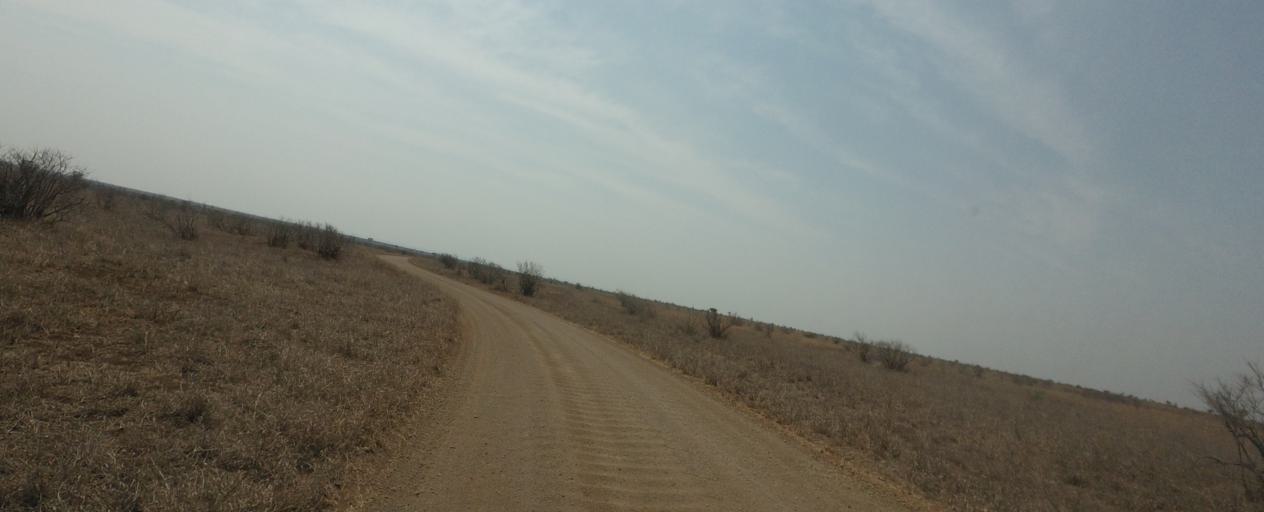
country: ZA
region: Limpopo
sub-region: Mopani District Municipality
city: Phalaborwa
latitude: -24.2542
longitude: 31.6994
